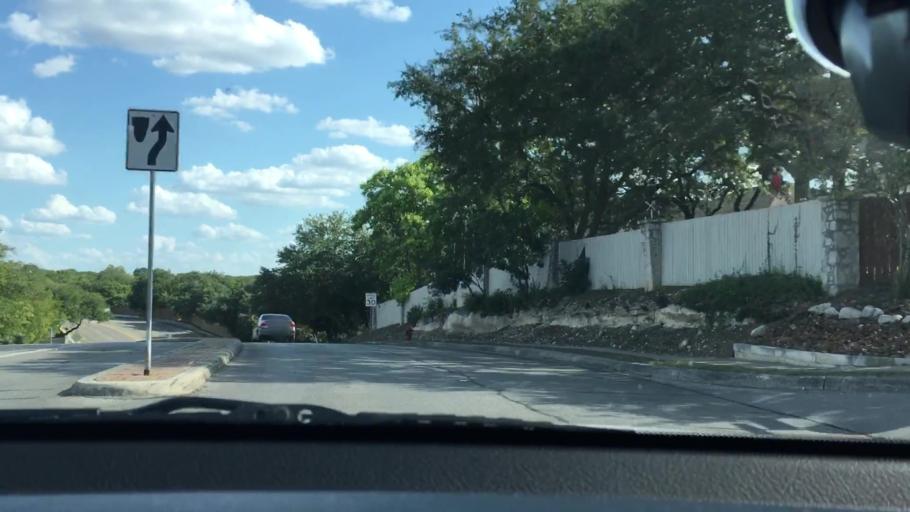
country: US
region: Texas
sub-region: Bexar County
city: Selma
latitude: 29.5632
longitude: -98.3129
